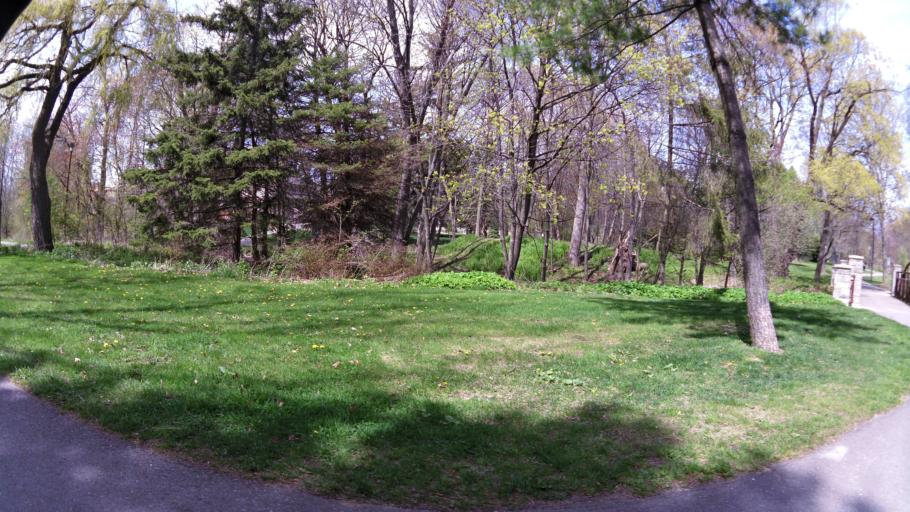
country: CA
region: Ontario
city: Mississauga
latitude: 43.5398
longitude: -79.5940
